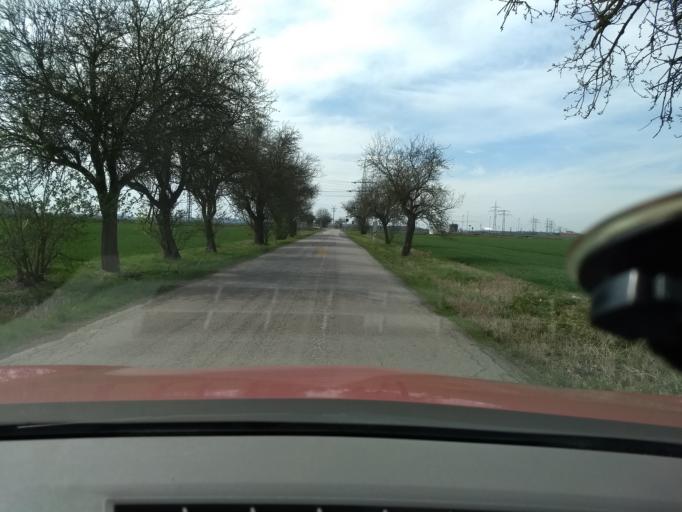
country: CZ
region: Central Bohemia
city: Rudna
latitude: 50.0514
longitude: 14.2235
